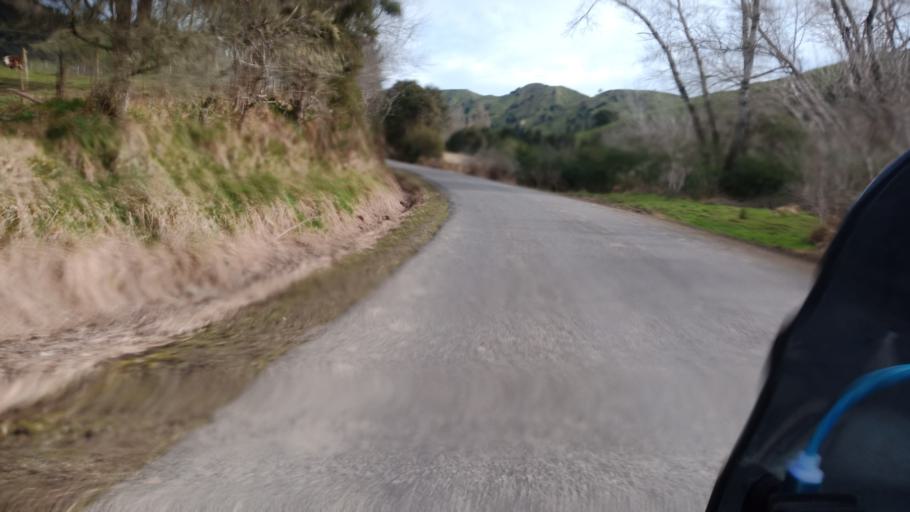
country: NZ
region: Hawke's Bay
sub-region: Wairoa District
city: Wairoa
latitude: -38.8003
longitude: 177.4556
